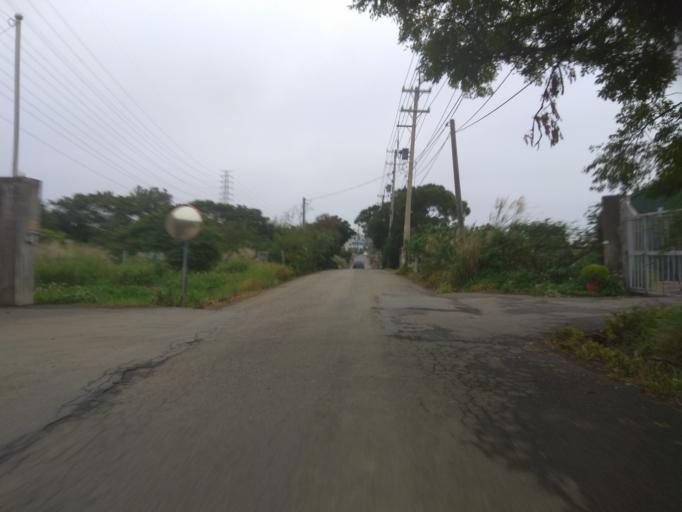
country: TW
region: Taiwan
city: Taoyuan City
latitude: 24.9936
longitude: 121.1246
